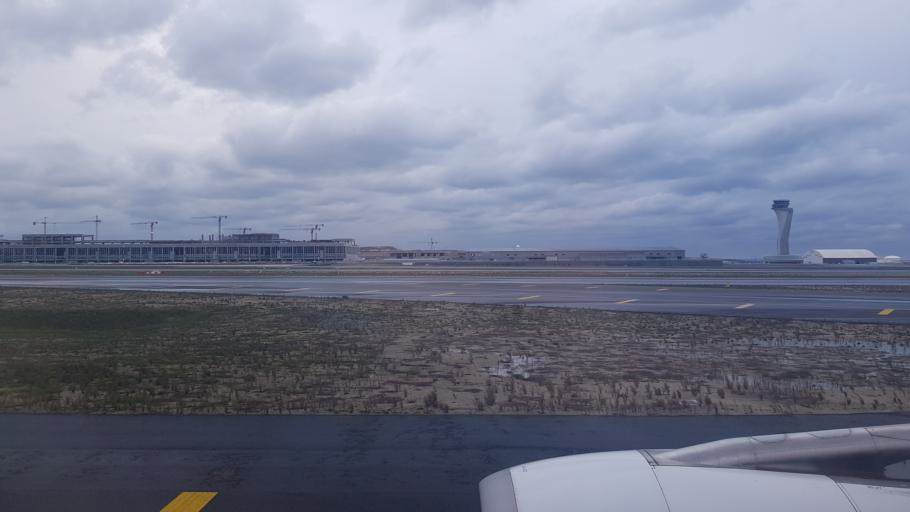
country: TR
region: Istanbul
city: Durusu
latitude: 41.2804
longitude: 28.7296
